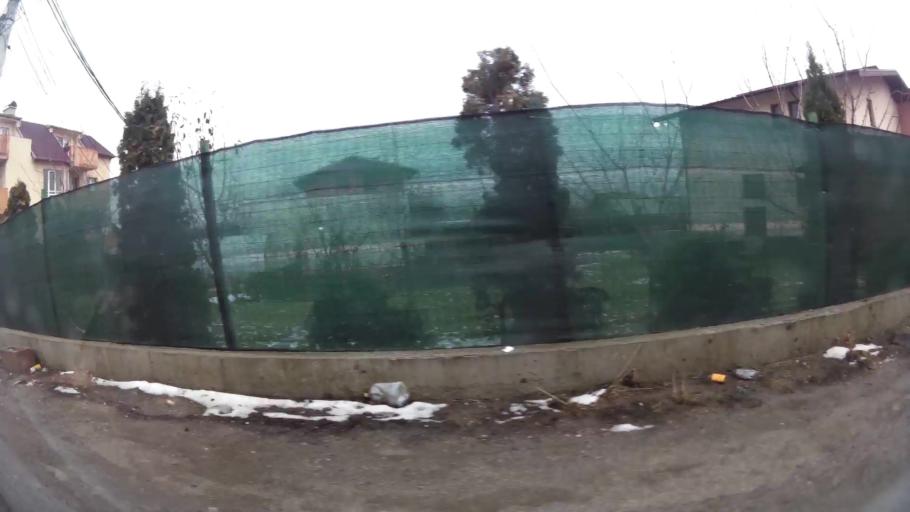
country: BG
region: Sofiya
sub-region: Obshtina Bozhurishte
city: Bozhurishte
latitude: 42.6826
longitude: 23.2342
